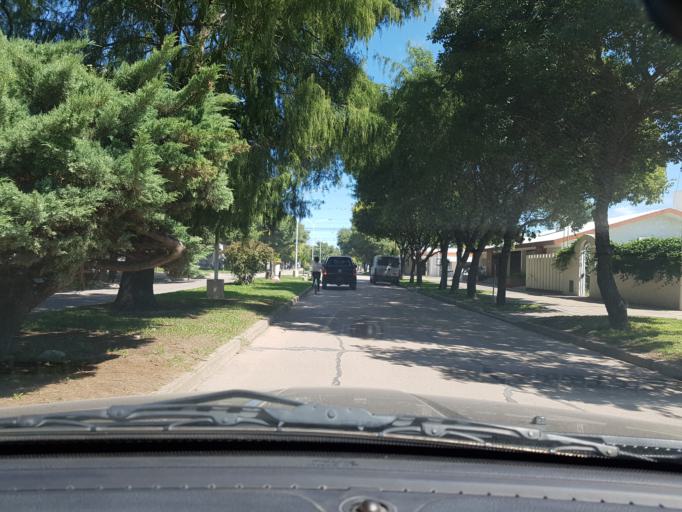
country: AR
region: Cordoba
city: General Cabrera
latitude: -32.7588
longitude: -63.7926
